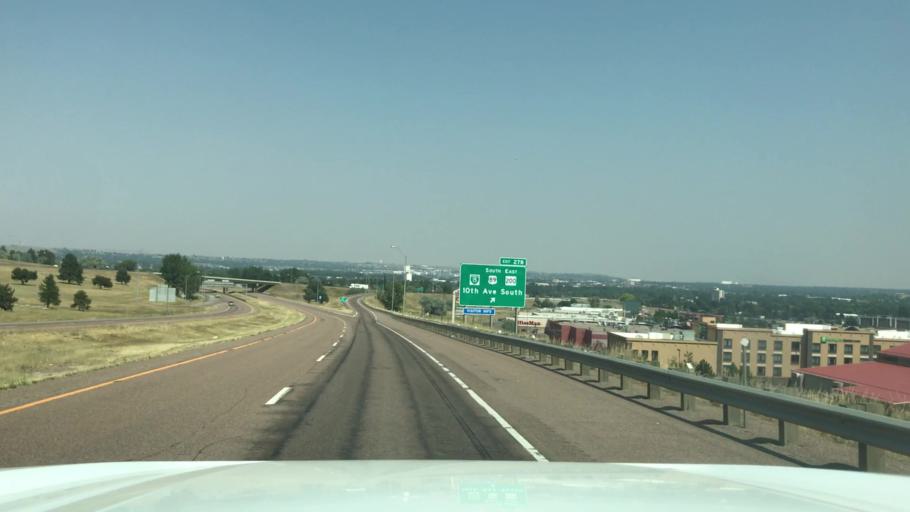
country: US
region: Montana
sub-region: Cascade County
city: Great Falls
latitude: 47.4808
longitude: -111.3483
